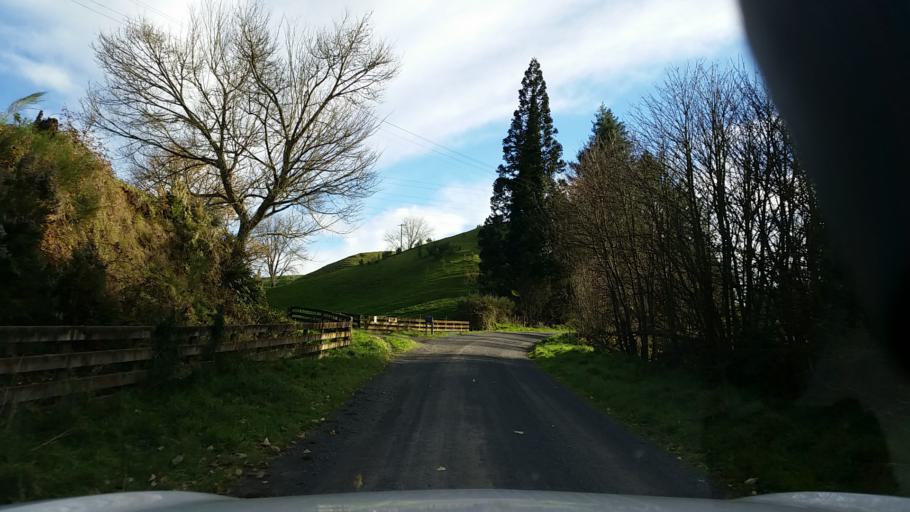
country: NZ
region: Waikato
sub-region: South Waikato District
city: Tokoroa
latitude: -38.3680
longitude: 176.0890
